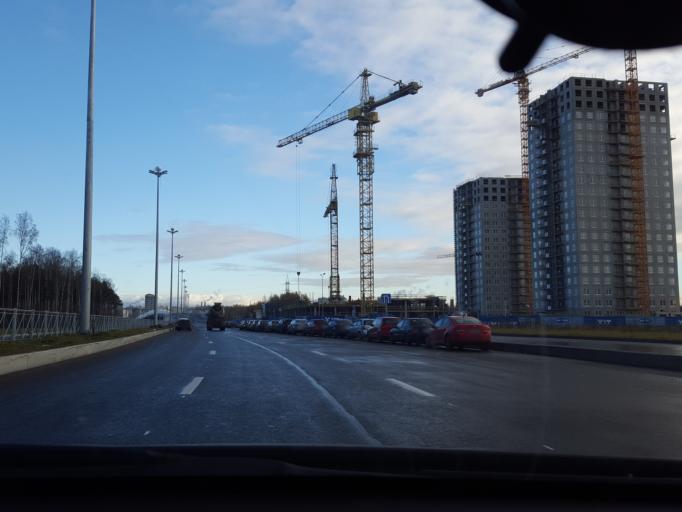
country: RU
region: St.-Petersburg
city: Pargolovo
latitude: 60.0586
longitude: 30.2673
